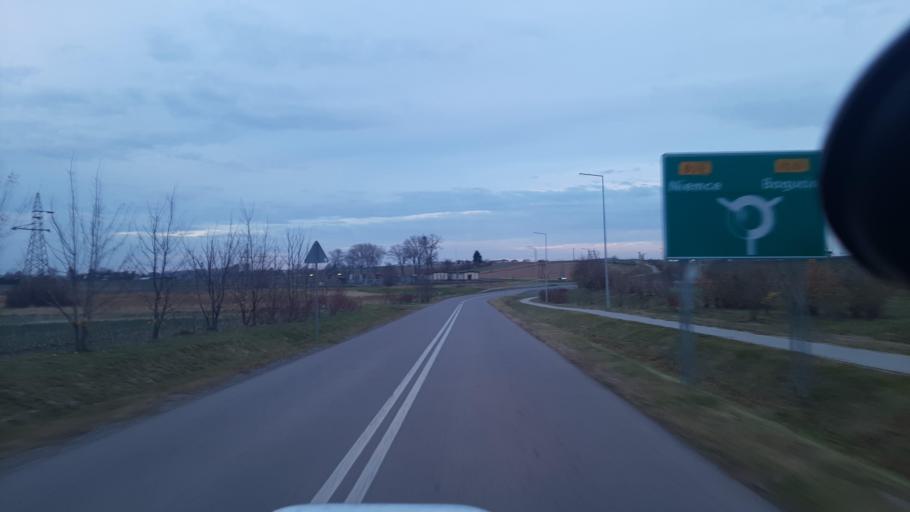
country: PL
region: Lublin Voivodeship
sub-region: Powiat lubelski
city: Garbow
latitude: 51.3498
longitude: 22.3688
